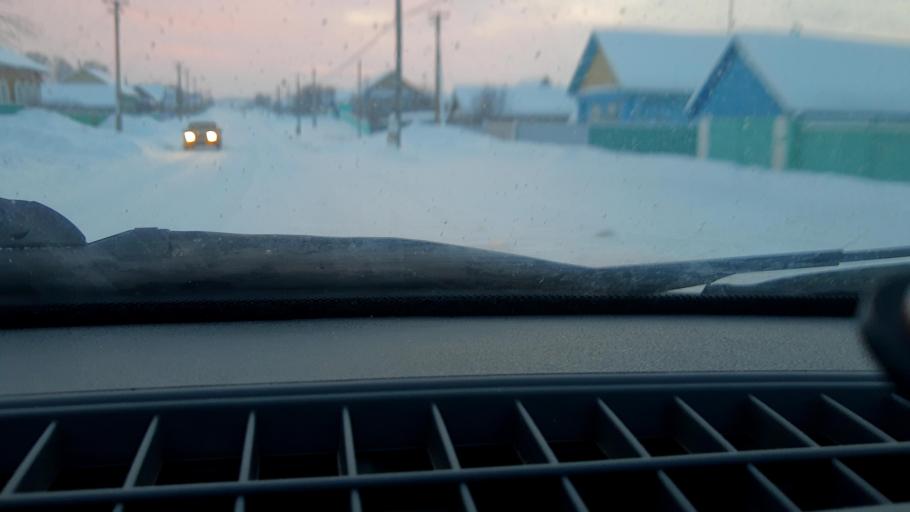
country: RU
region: Bashkortostan
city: Davlekanovo
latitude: 54.5390
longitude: 55.0447
